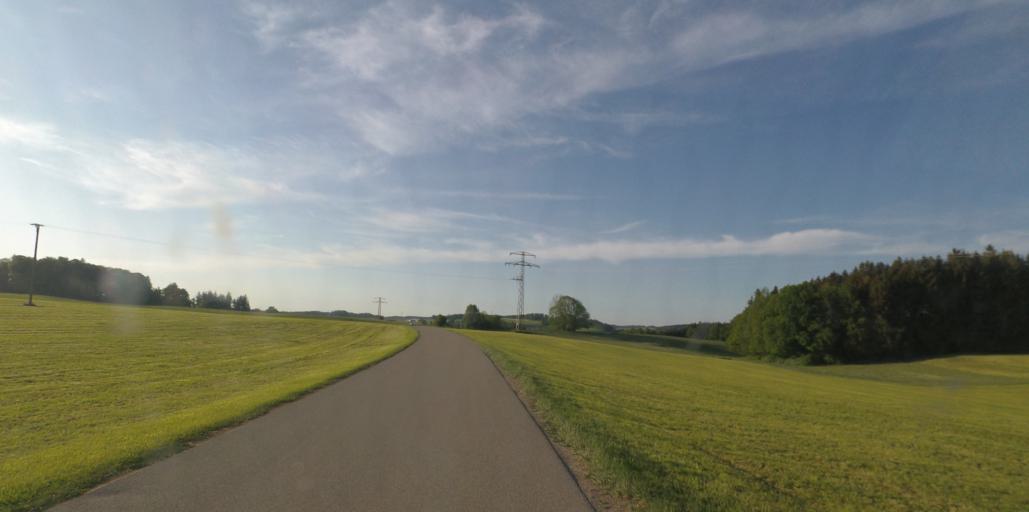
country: DE
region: Bavaria
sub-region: Upper Bavaria
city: Bergen
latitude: 47.8383
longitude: 12.5879
